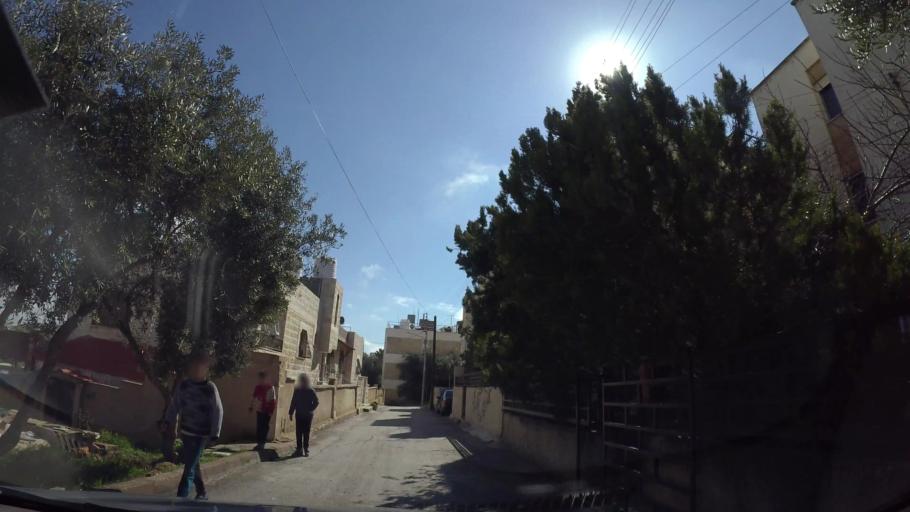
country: JO
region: Amman
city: Al Jubayhah
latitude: 32.0578
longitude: 35.8810
